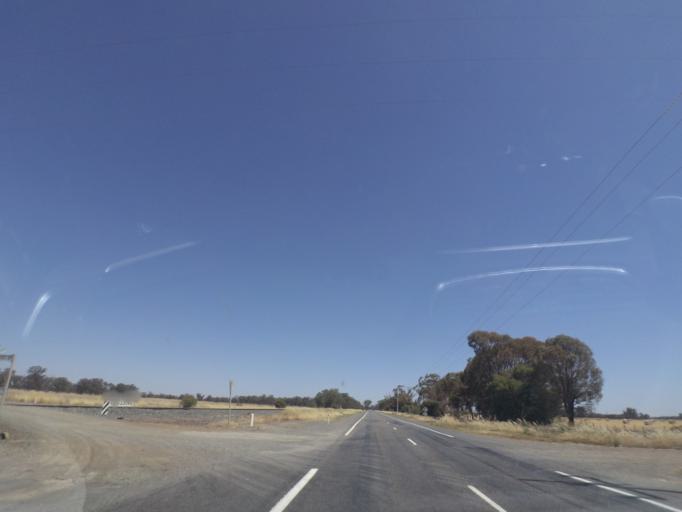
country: AU
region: Victoria
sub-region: Greater Shepparton
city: Shepparton
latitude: -36.2199
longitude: 145.4318
